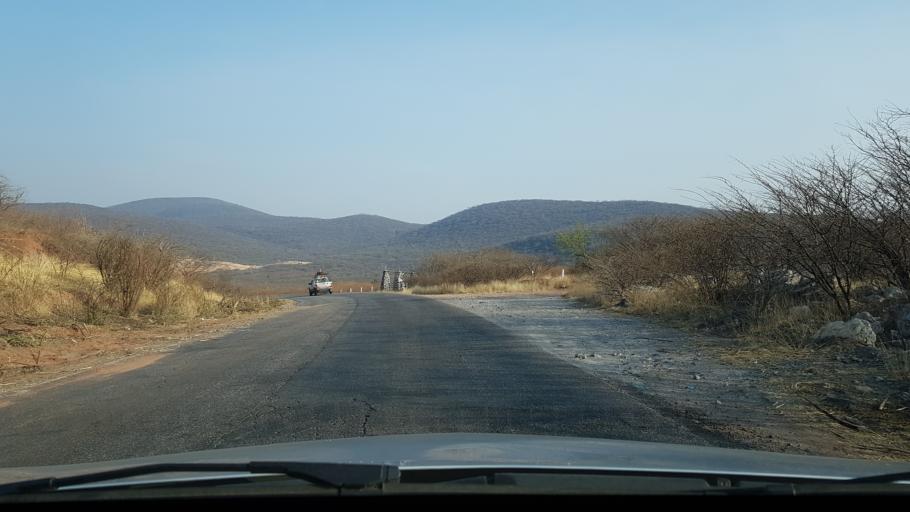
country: MX
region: Morelos
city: Tlaltizapan
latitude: 18.6696
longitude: -99.0539
